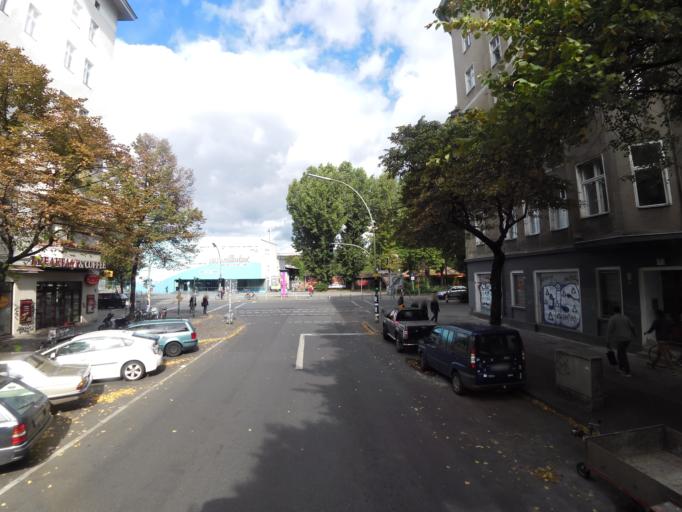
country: DE
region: Berlin
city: Berlin Treptow
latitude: 52.4970
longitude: 13.4318
